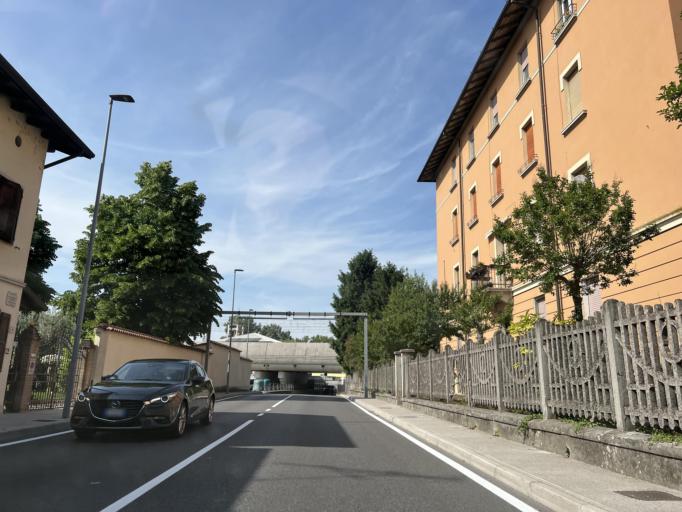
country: IT
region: Friuli Venezia Giulia
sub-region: Provincia di Udine
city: Cervignano del Friuli
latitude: 45.8241
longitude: 13.3383
